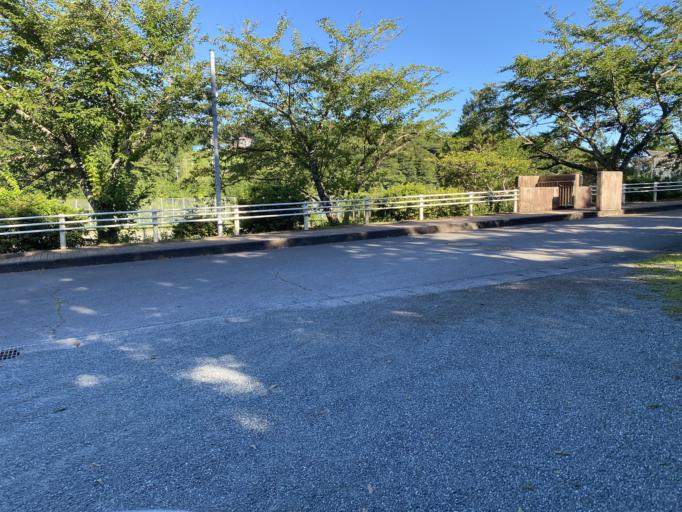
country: JP
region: Shizuoka
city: Gotemba
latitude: 35.2488
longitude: 138.9237
